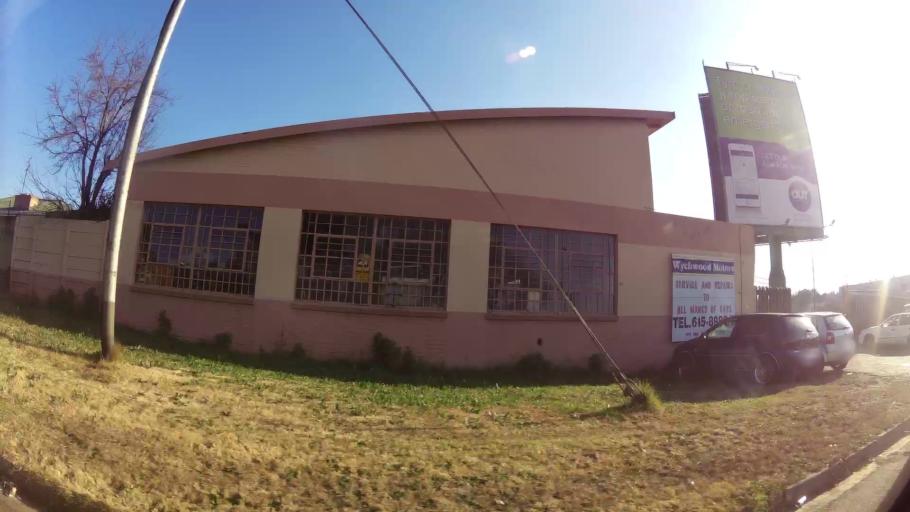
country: ZA
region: Gauteng
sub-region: Ekurhuleni Metropolitan Municipality
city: Germiston
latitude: -26.1998
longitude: 28.1325
